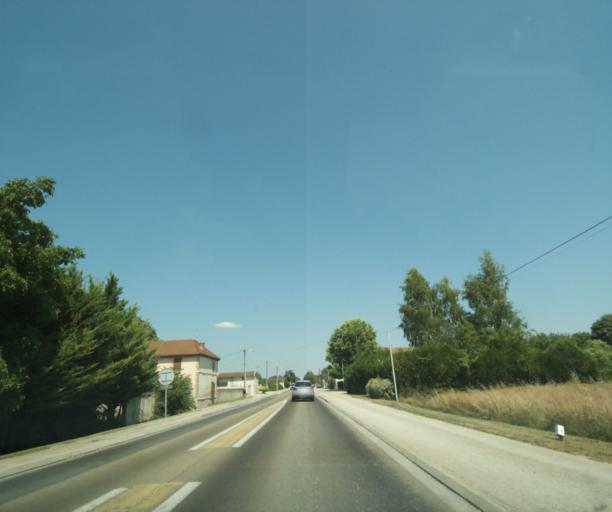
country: FR
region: Champagne-Ardenne
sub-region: Departement de la Marne
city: Sarry
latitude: 48.9016
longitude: 4.4405
